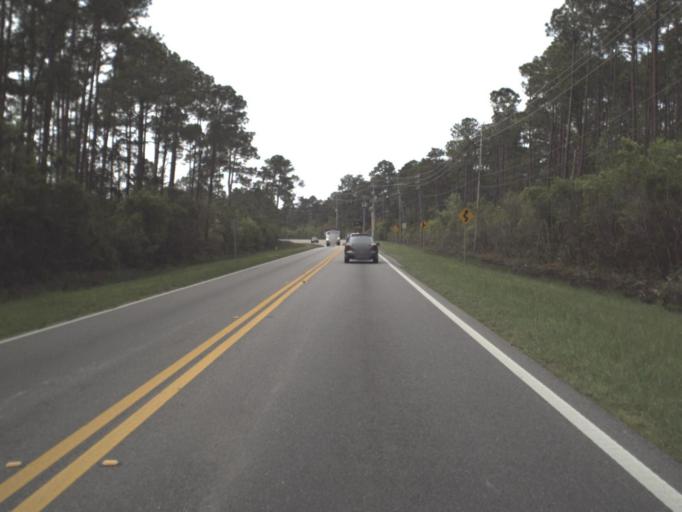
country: US
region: Florida
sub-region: Escambia County
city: Myrtle Grove
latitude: 30.3294
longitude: -87.4149
